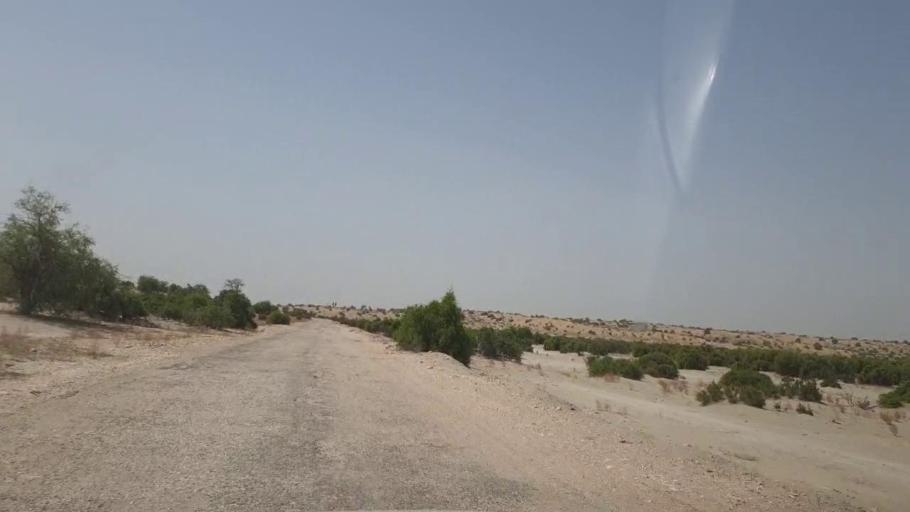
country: PK
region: Sindh
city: Khanpur
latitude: 27.3555
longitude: 69.3179
